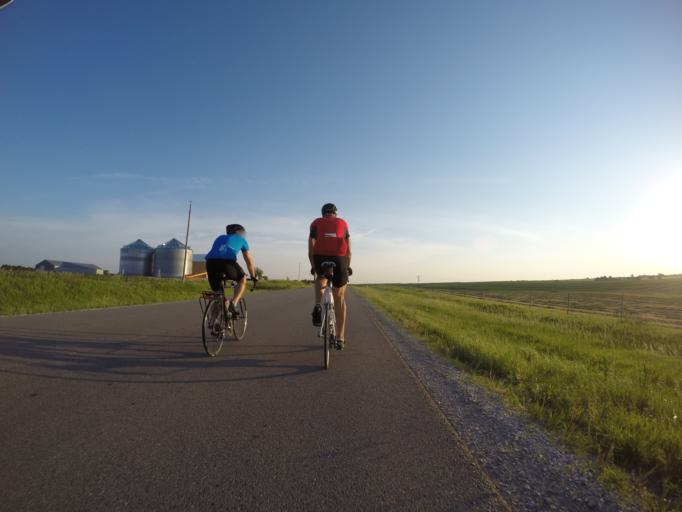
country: US
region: Kansas
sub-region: Marshall County
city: Marysville
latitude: 39.8544
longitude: -96.6009
